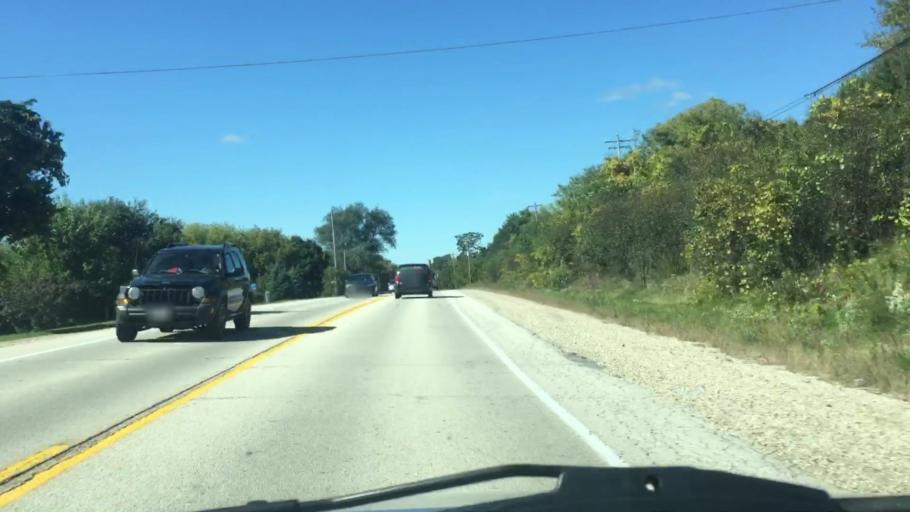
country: US
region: Wisconsin
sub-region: Waukesha County
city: Wales
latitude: 43.0202
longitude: -88.3499
